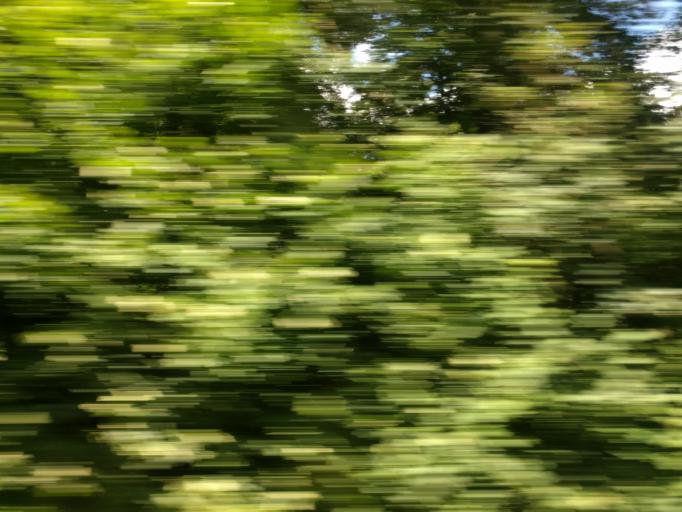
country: DK
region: Zealand
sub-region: Roskilde Kommune
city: Viby
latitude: 55.5292
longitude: 11.9918
